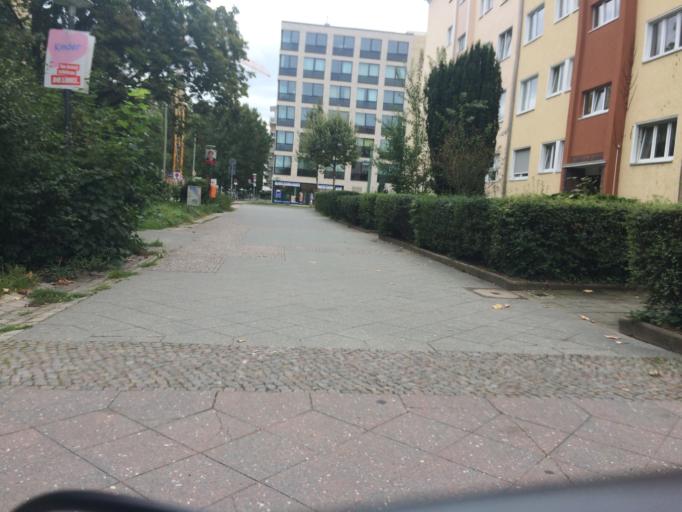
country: DE
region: Berlin
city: Gesundbrunnen
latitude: 52.5400
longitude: 13.3996
